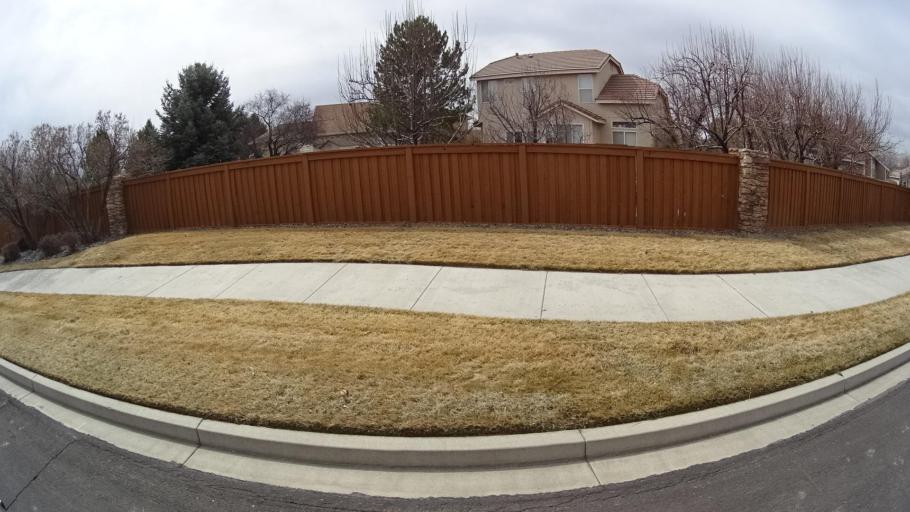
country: US
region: Nevada
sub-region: Washoe County
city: Spanish Springs
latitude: 39.6310
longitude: -119.6861
